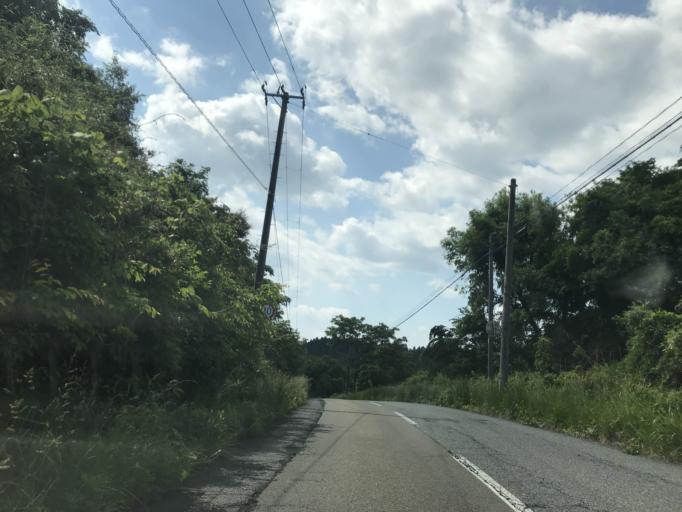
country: JP
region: Miyagi
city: Furukawa
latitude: 38.7764
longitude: 140.9599
